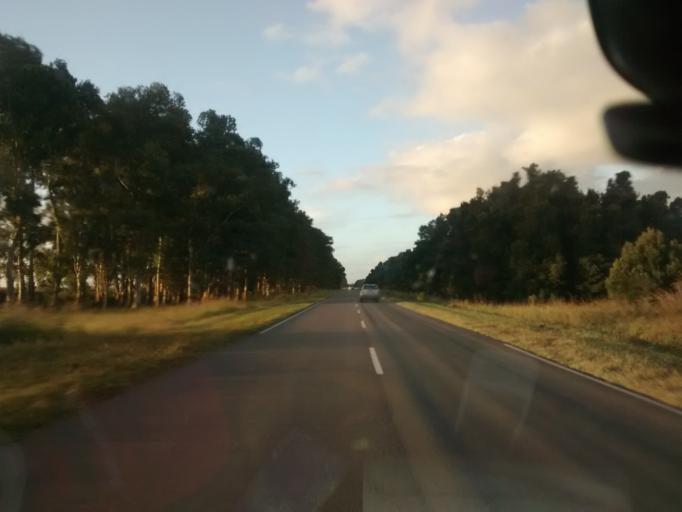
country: AR
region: Buenos Aires
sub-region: Partido de General Belgrano
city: General Belgrano
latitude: -35.6670
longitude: -58.4752
